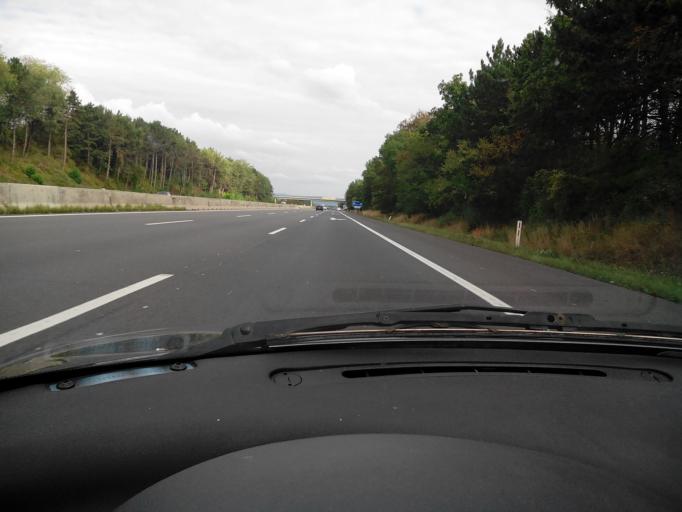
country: AT
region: Lower Austria
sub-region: Politischer Bezirk Baden
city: Leobersdorf
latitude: 47.9042
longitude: 16.2079
